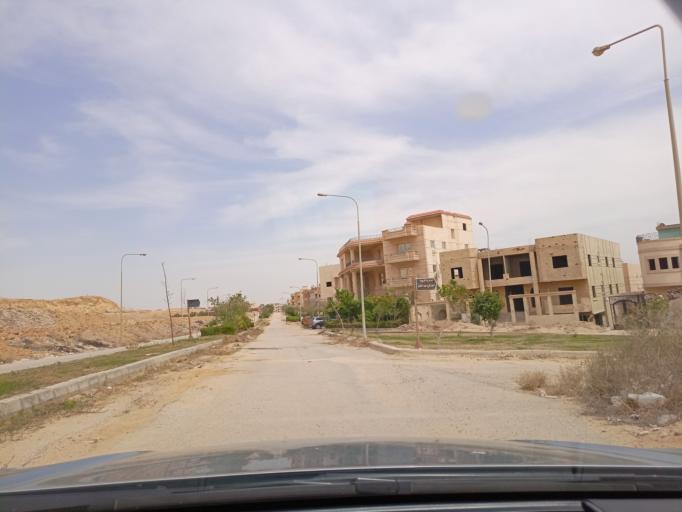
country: EG
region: Muhafazat al Qalyubiyah
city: Al Khankah
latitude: 30.2407
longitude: 31.4909
